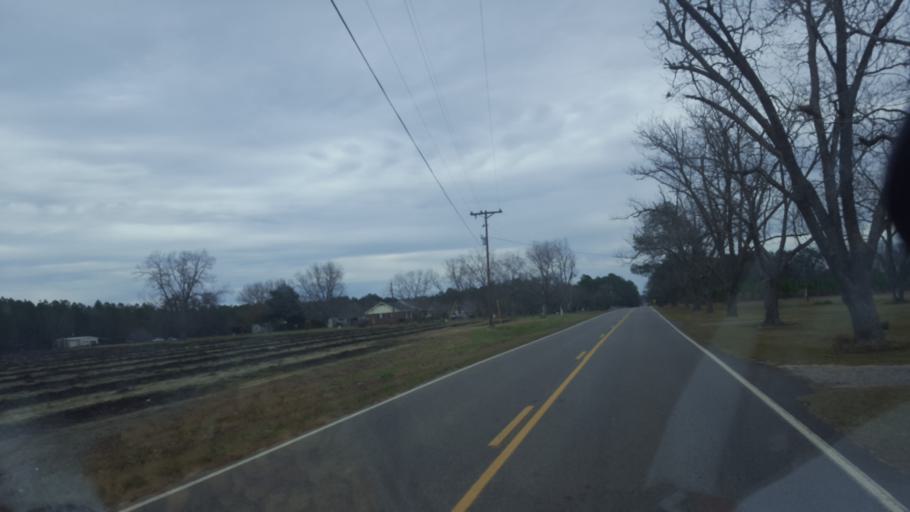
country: US
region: Georgia
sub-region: Ben Hill County
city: Fitzgerald
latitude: 31.7436
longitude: -83.2776
